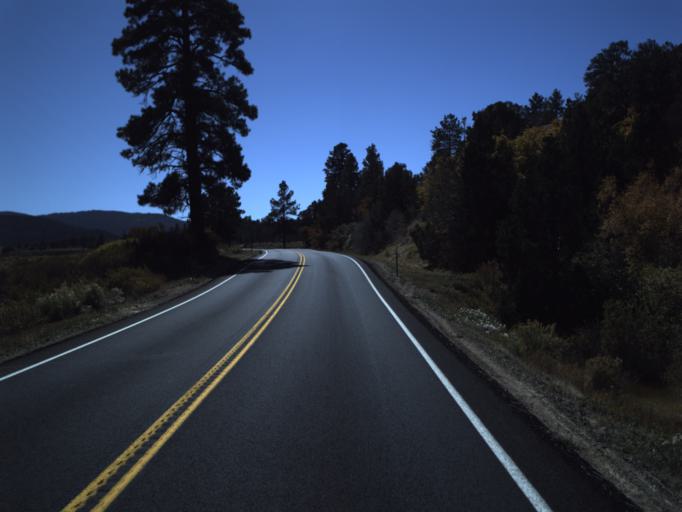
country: US
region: Utah
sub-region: Garfield County
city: Panguitch
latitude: 37.7160
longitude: -111.7845
